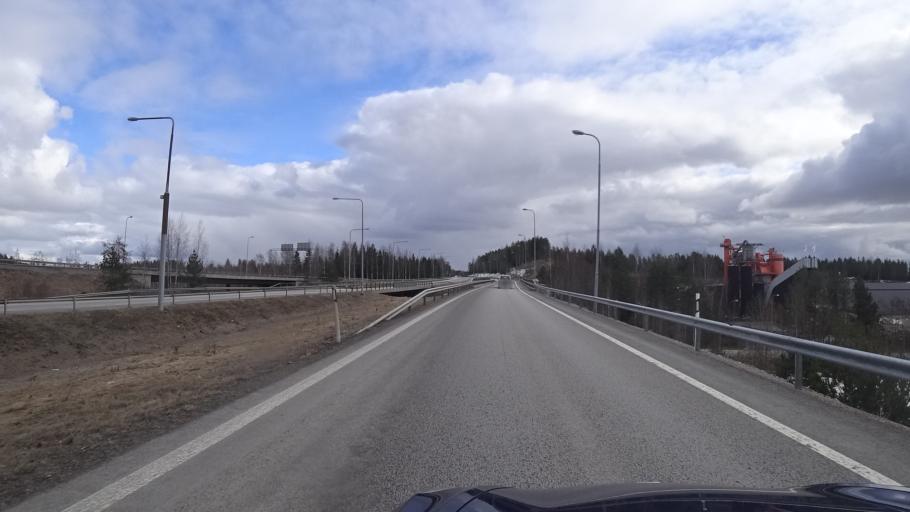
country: FI
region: Paijanne Tavastia
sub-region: Lahti
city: Lahti
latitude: 60.9695
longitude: 25.7245
